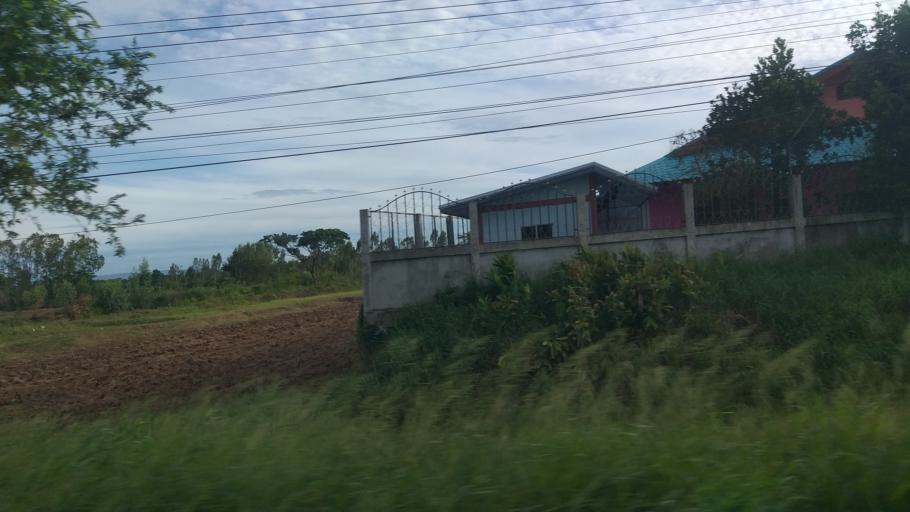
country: TH
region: Chaiyaphum
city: Ban Thaen
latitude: 16.3825
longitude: 102.3111
